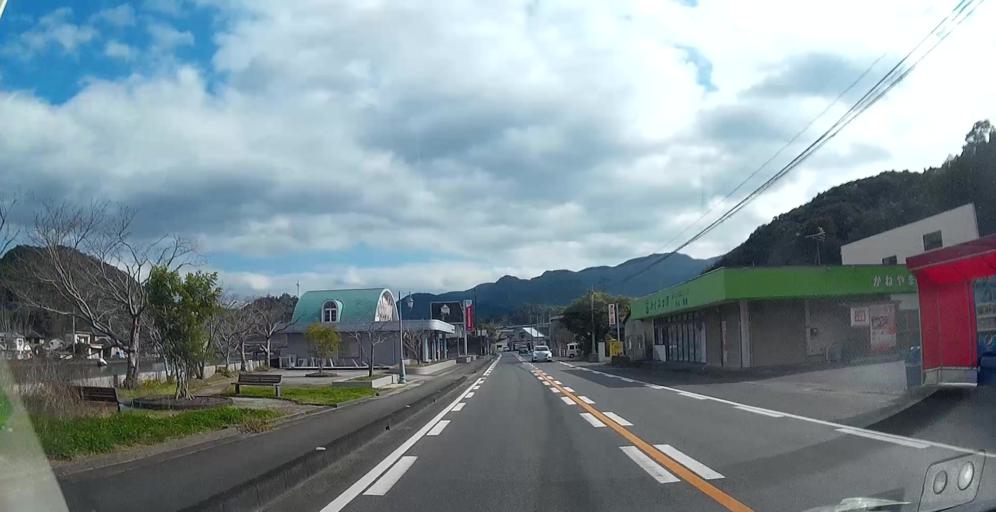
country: JP
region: Kumamoto
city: Minamata
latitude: 32.2341
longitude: 130.4457
